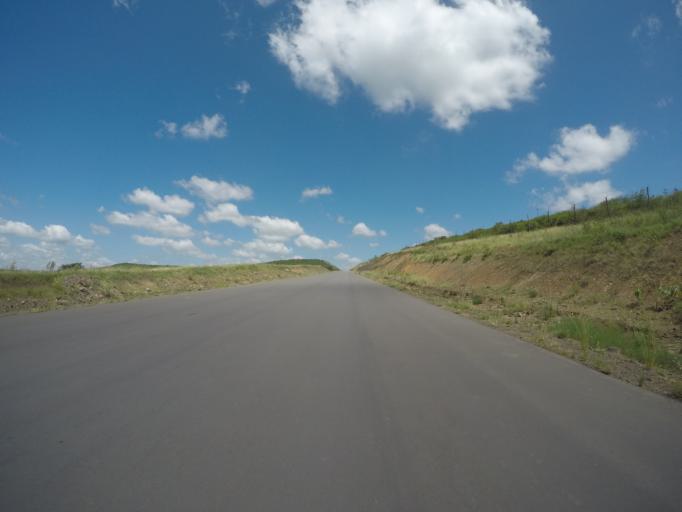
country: ZA
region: KwaZulu-Natal
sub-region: uThungulu District Municipality
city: Empangeni
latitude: -28.6210
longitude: 31.7566
